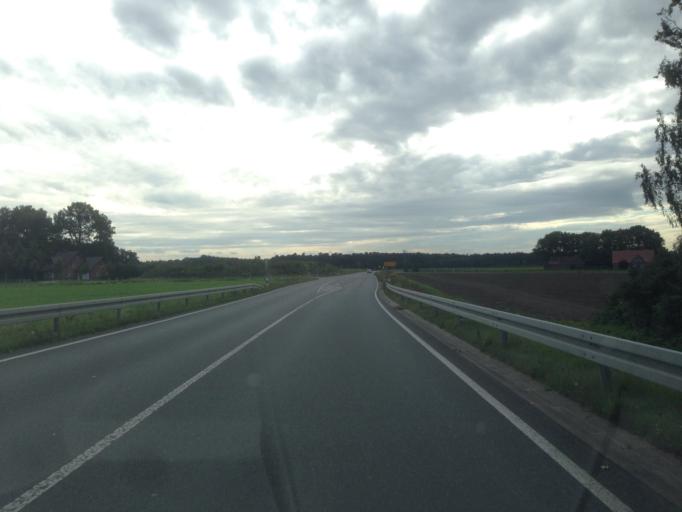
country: DE
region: North Rhine-Westphalia
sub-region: Regierungsbezirk Munster
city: Dulmen
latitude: 51.8051
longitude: 7.3409
